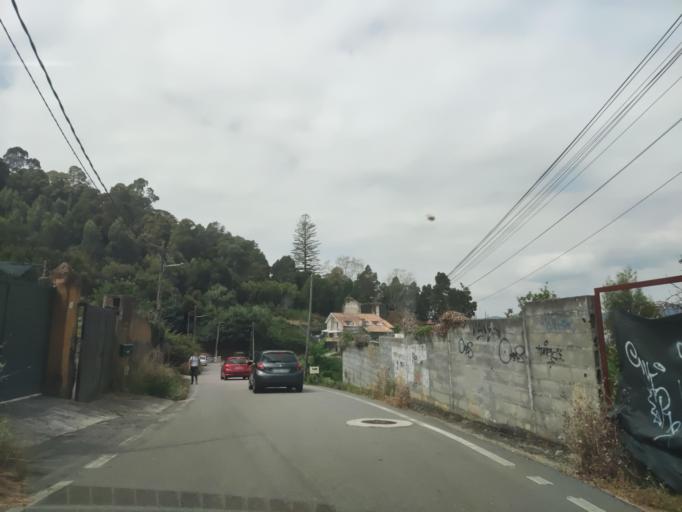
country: ES
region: Galicia
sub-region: Provincia de Pontevedra
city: Vigo
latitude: 42.2585
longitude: -8.6989
